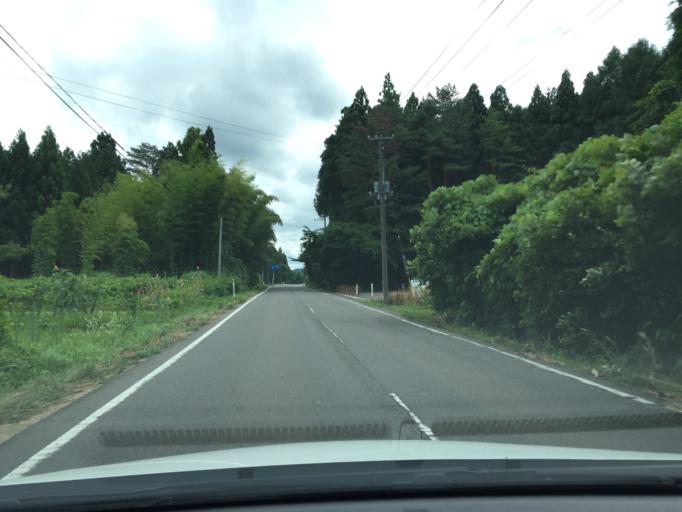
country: JP
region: Fukushima
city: Sukagawa
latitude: 37.2847
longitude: 140.1699
